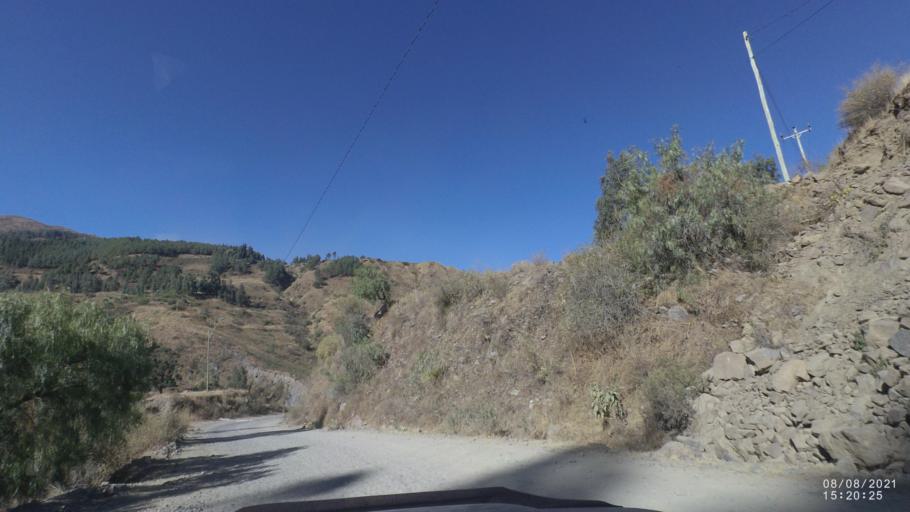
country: BO
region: Cochabamba
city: Cochabamba
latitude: -17.2964
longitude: -66.2979
